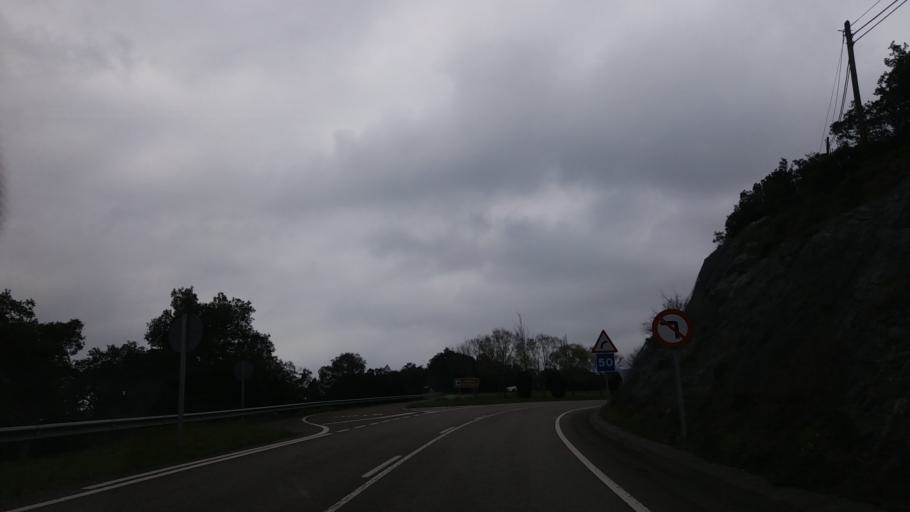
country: ES
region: Cantabria
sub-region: Provincia de Cantabria
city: San Vicente de la Barquera
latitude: 43.3303
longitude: -4.4929
